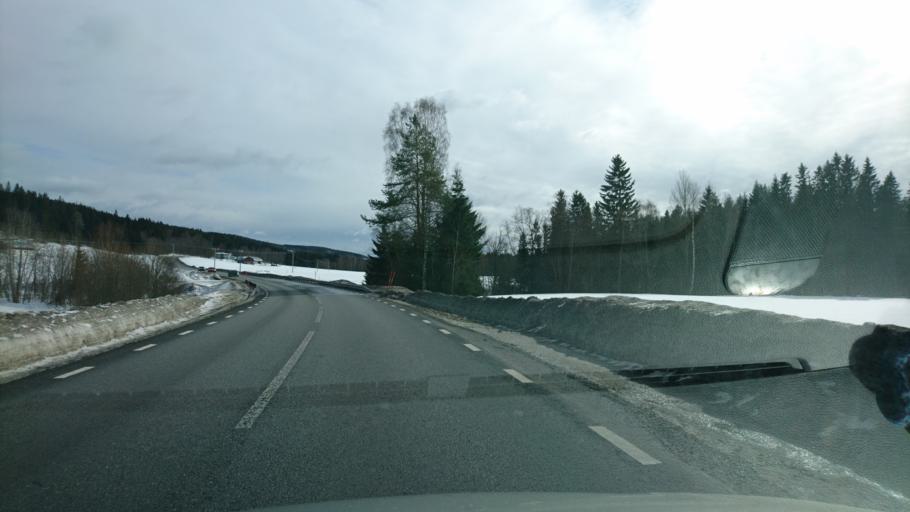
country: SE
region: Vaesternorrland
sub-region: Timra Kommun
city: Bergeforsen
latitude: 62.6000
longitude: 17.4085
